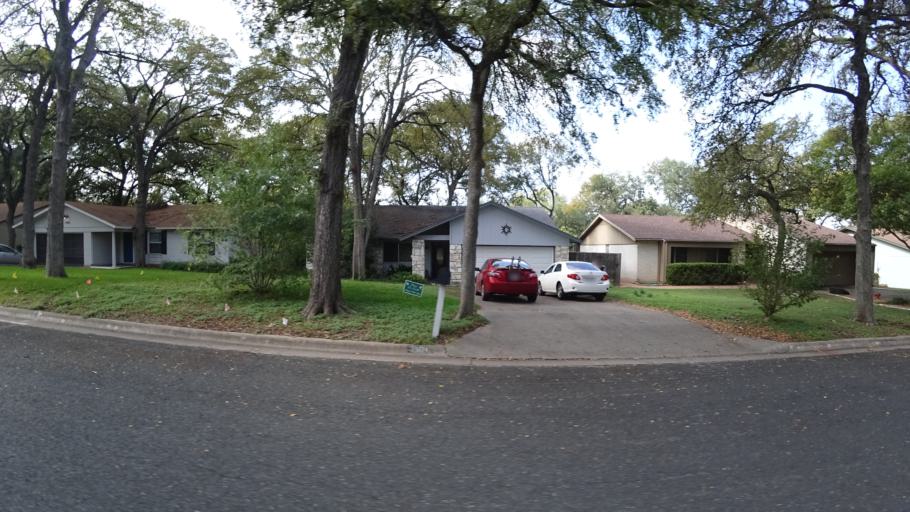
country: US
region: Texas
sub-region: Travis County
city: Shady Hollow
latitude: 30.2015
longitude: -97.8177
